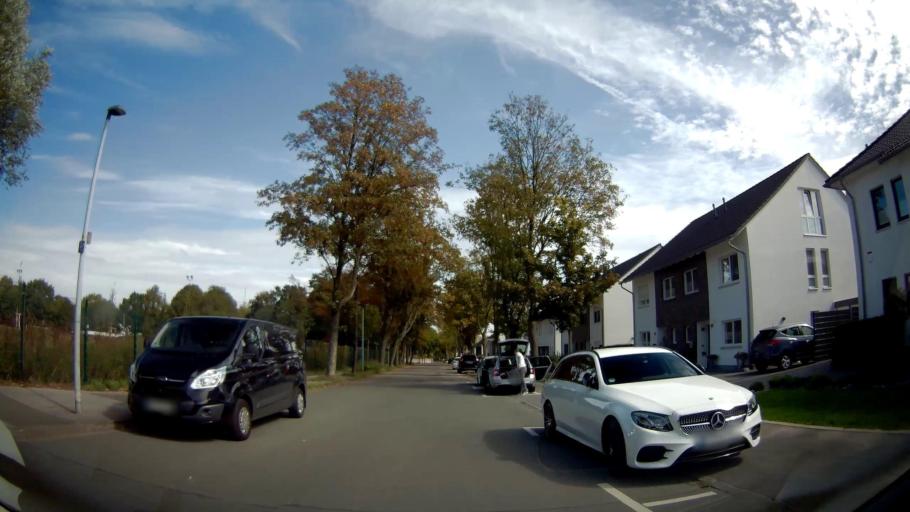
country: DE
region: North Rhine-Westphalia
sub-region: Regierungsbezirk Munster
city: Gladbeck
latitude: 51.5494
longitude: 7.0312
